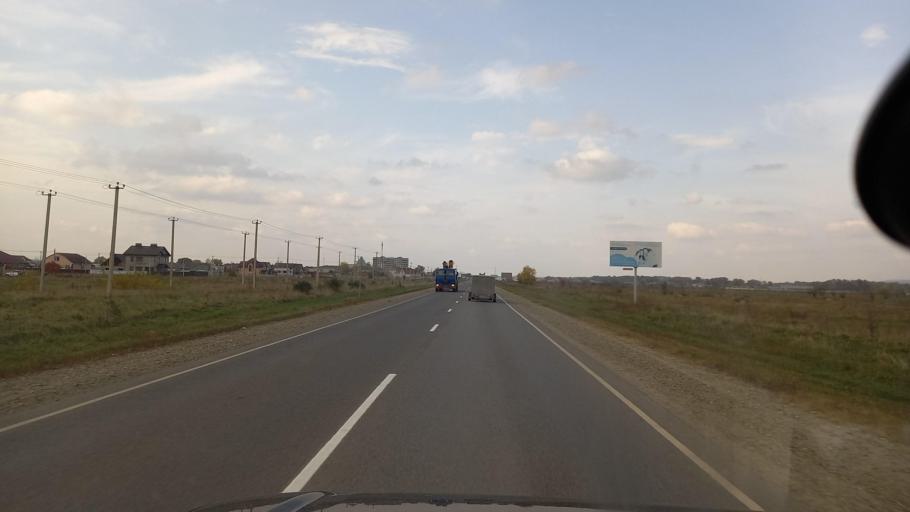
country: RU
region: Krasnodarskiy
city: Mostovskoy
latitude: 44.3844
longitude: 40.8193
